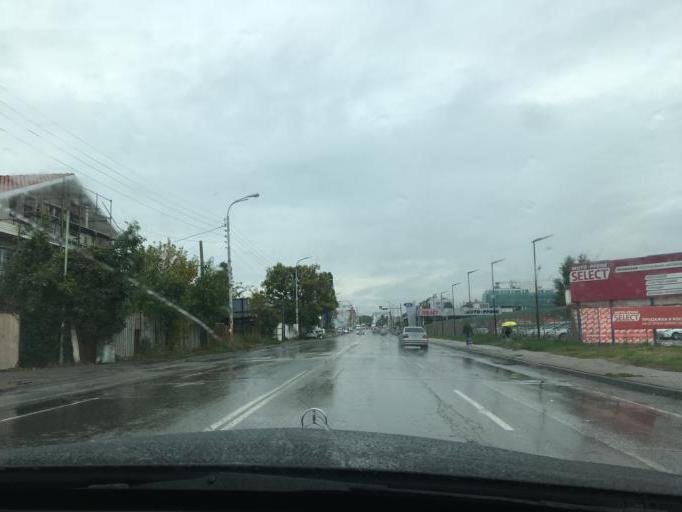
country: BG
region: Sofiya
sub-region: Obshtina Bozhurishte
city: Bozhurishte
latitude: 42.7287
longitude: 23.2585
